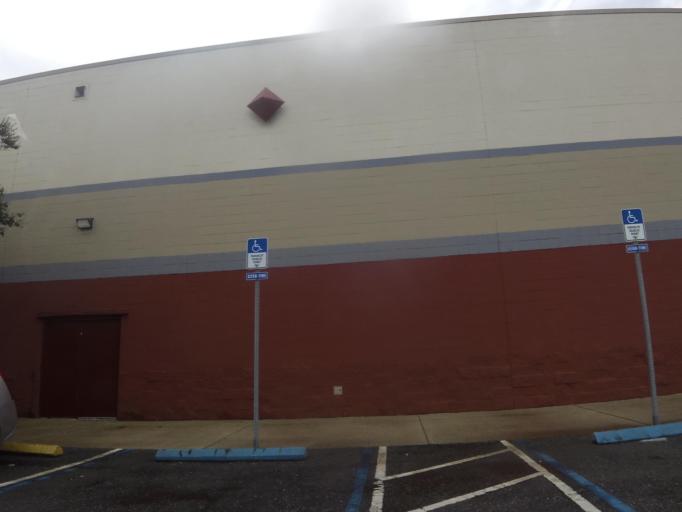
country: US
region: Florida
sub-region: Duval County
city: Atlantic Beach
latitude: 30.3178
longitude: -81.4867
